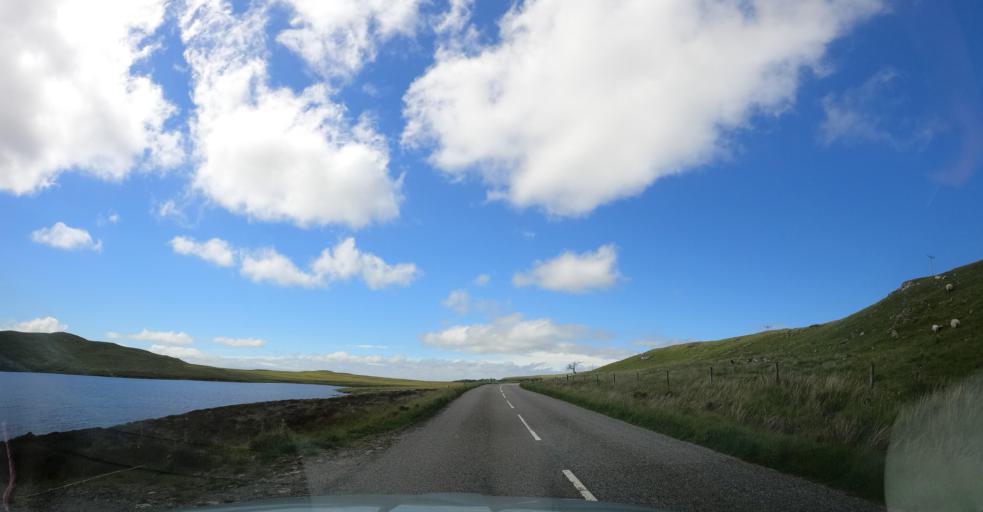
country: GB
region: Scotland
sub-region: Eilean Siar
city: Stornoway
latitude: 58.1600
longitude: -6.5313
